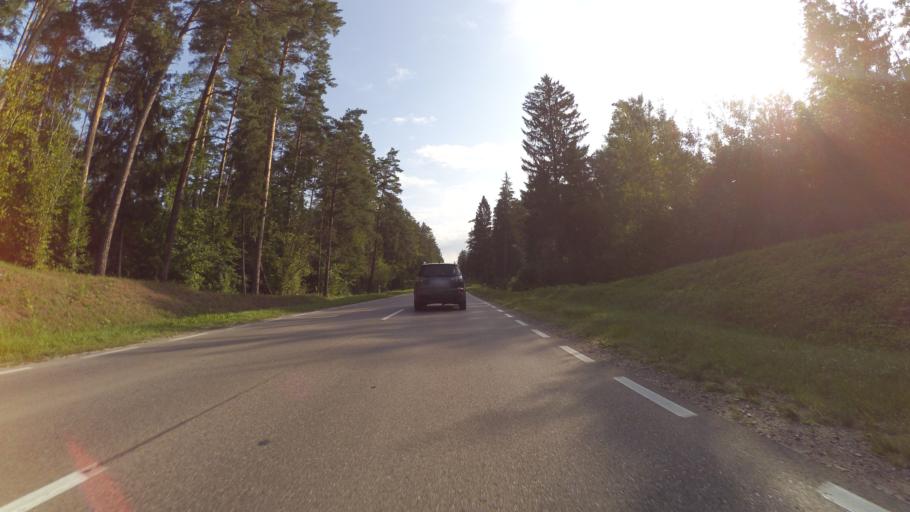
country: PL
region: Podlasie
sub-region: Powiat bialostocki
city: Czarna Bialostocka
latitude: 53.3214
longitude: 23.3410
